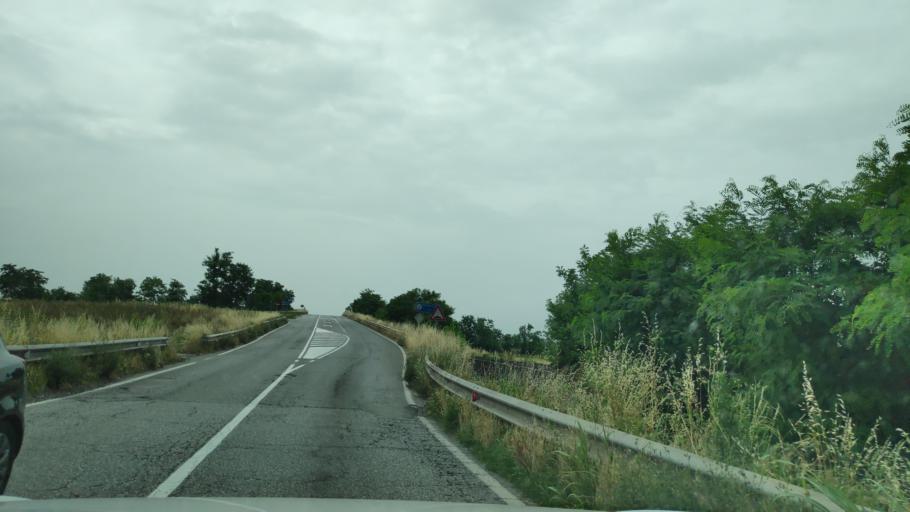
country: IT
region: Lombardy
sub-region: Provincia di Brescia
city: Orzinuovi
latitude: 45.4124
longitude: 9.9273
